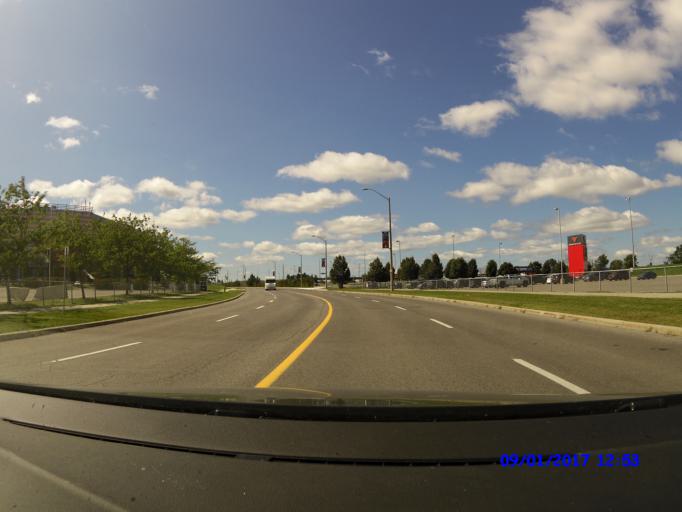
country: CA
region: Ontario
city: Bells Corners
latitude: 45.2990
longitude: -75.9249
